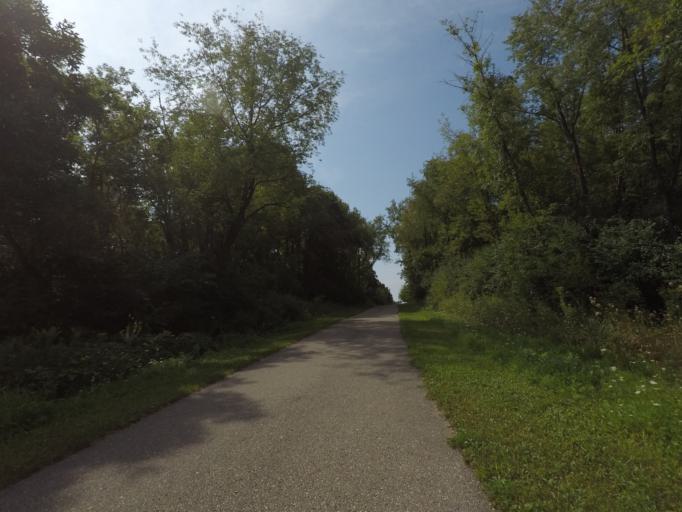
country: US
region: Wisconsin
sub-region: Jefferson County
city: Fort Atkinson
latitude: 42.9546
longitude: -88.8277
